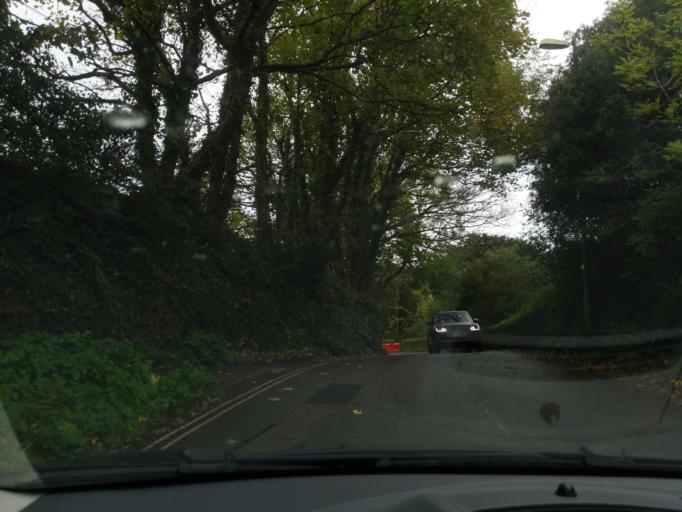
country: GB
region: England
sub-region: Cornwall
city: Padstow
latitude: 50.5406
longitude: -4.9462
